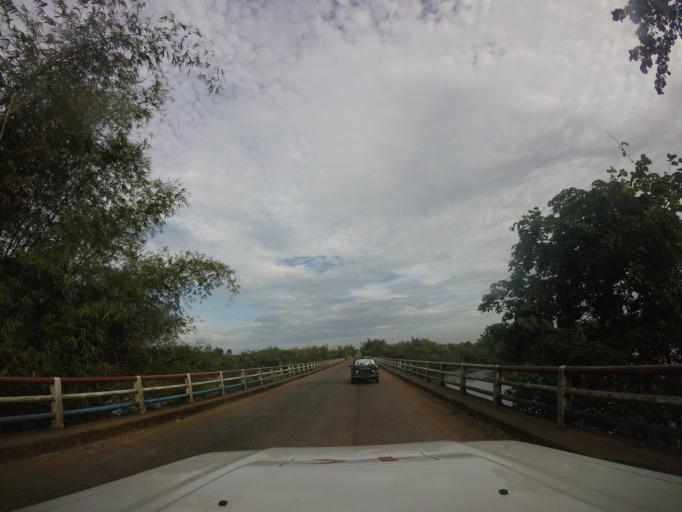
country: LR
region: Bomi
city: Tubmanburg
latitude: 6.7208
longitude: -10.9795
